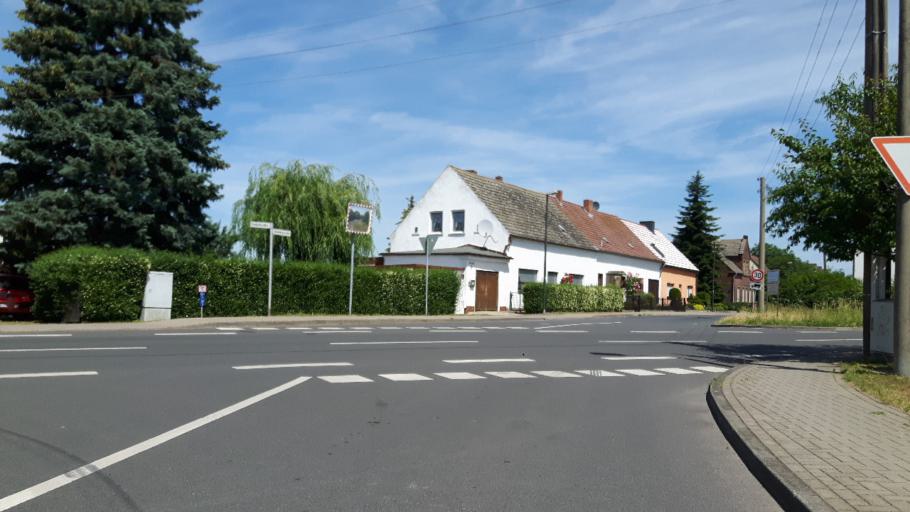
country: DE
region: Saxony-Anhalt
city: Wittenburg
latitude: 51.8886
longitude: 12.6420
